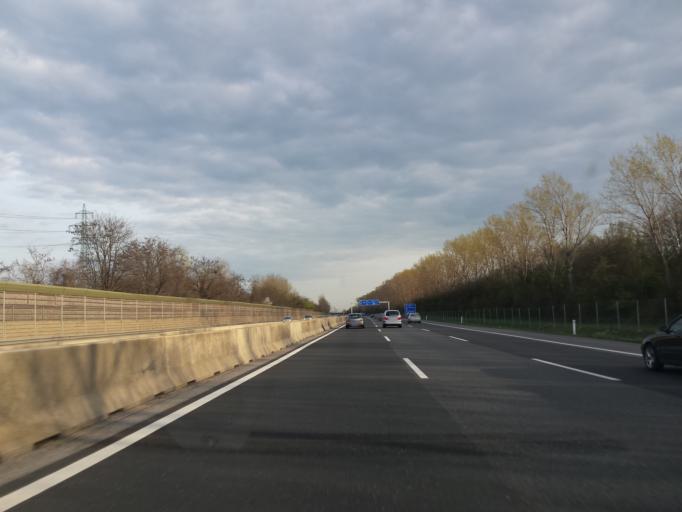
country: AT
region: Lower Austria
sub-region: Politischer Bezirk Korneuburg
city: Langenzersdorf
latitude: 48.2934
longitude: 16.3549
